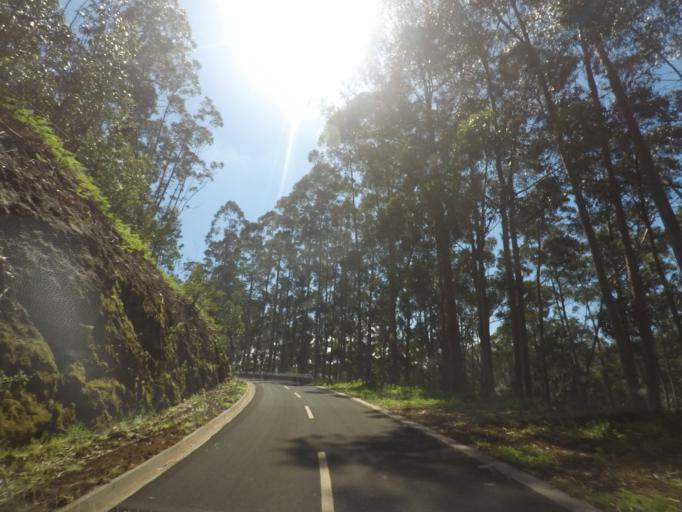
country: PT
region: Madeira
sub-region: Calheta
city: Arco da Calheta
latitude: 32.7265
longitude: -17.1227
